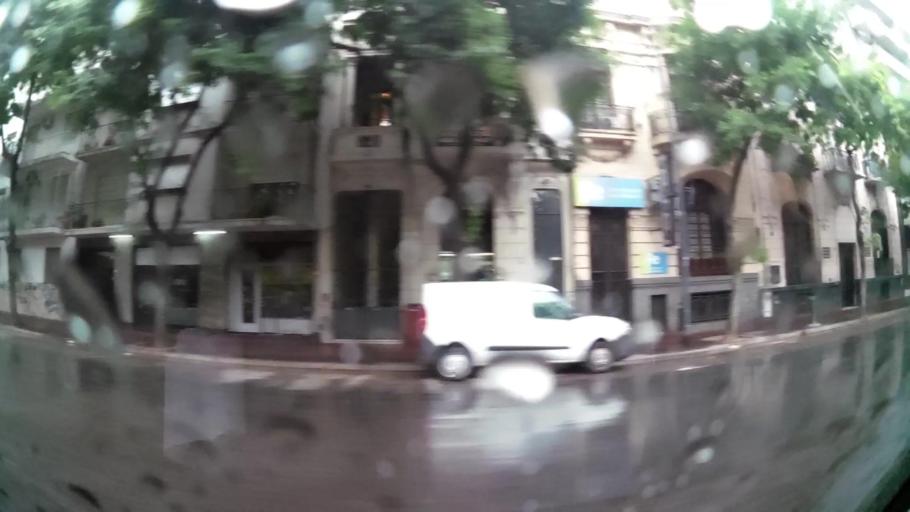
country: AR
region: Buenos Aires F.D.
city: Buenos Aires
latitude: -34.6243
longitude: -58.3721
